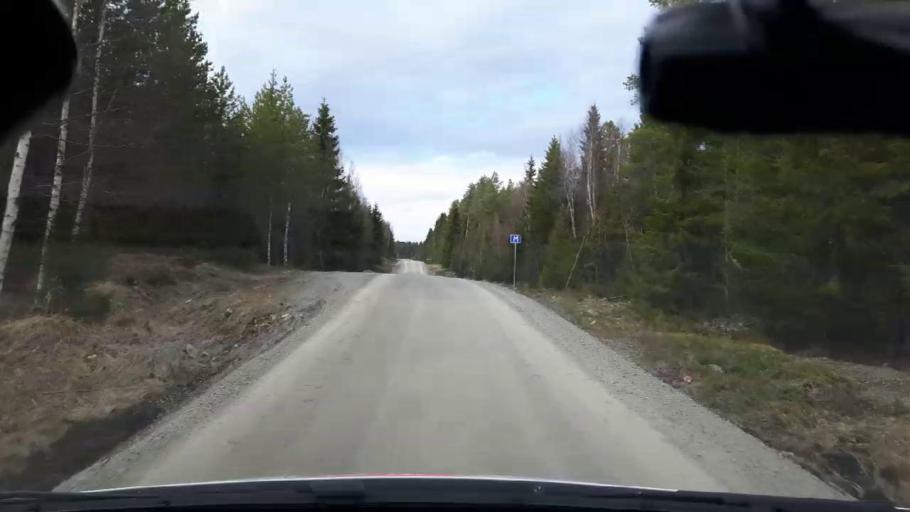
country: SE
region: Jaemtland
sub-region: OEstersunds Kommun
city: Brunflo
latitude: 62.9368
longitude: 14.6643
